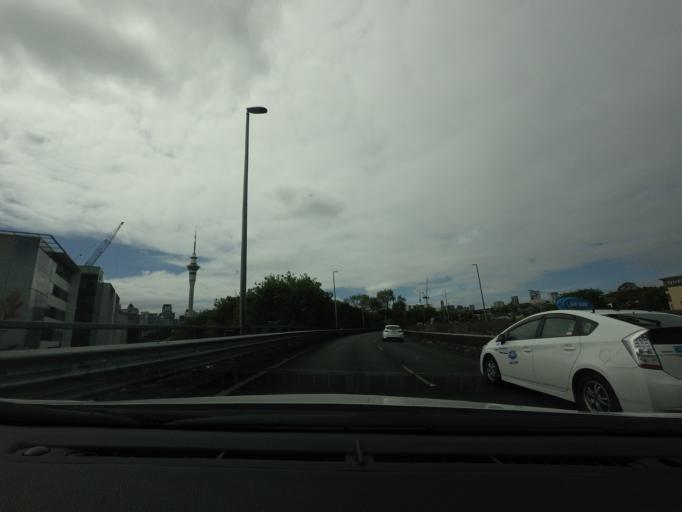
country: NZ
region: Auckland
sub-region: Auckland
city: Auckland
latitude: -36.8450
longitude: 174.7526
